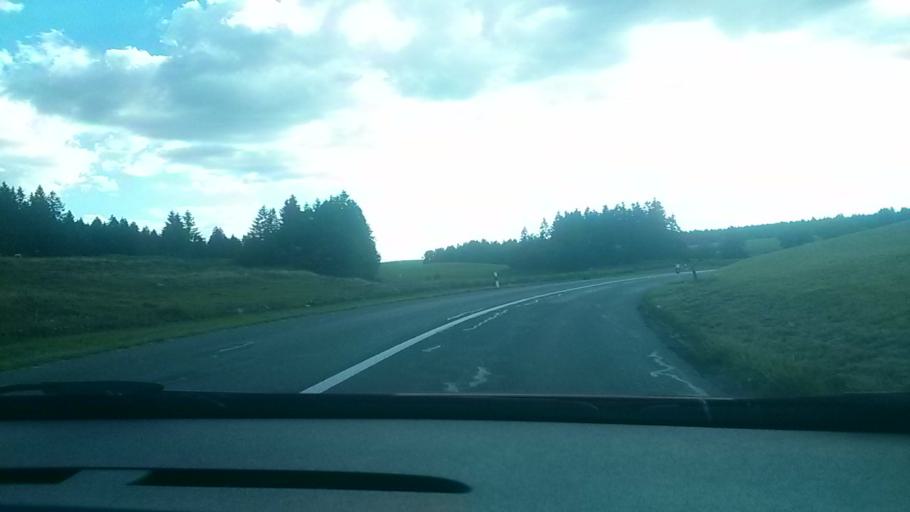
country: CH
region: Vaud
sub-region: Jura-Nord vaudois District
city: L'Abbaye
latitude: 46.6405
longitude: 6.2715
